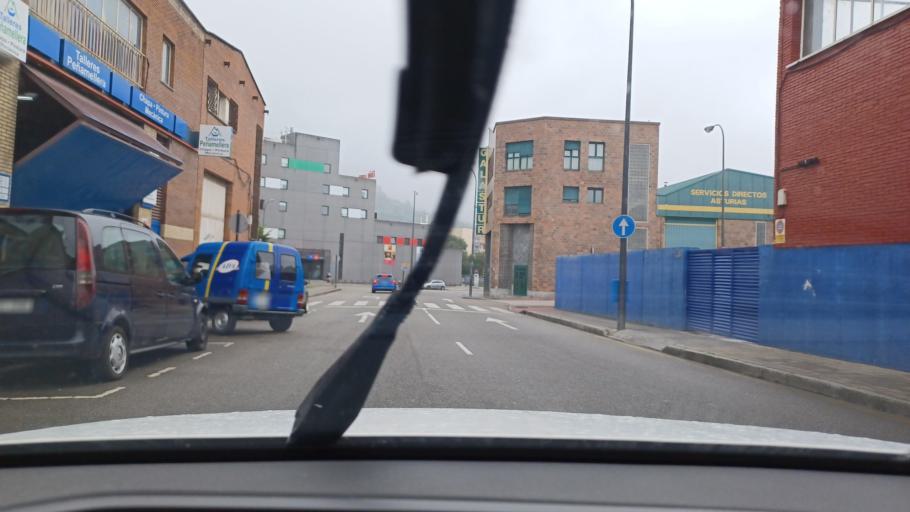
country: ES
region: Asturias
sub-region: Province of Asturias
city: Oviedo
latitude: 43.3728
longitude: -5.8505
